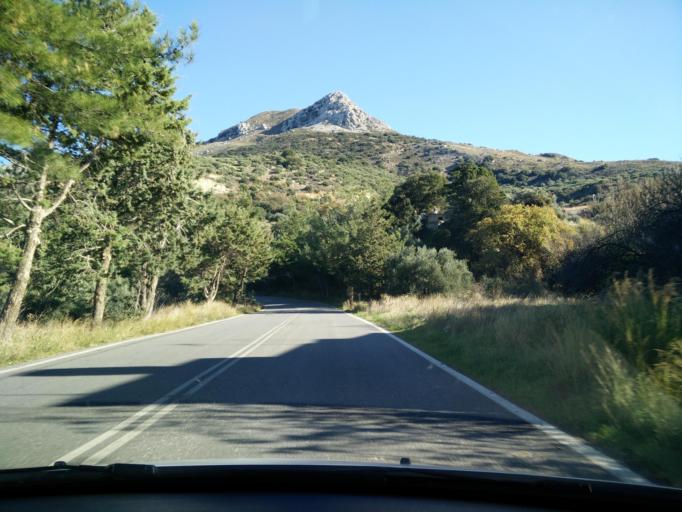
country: GR
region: Crete
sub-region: Nomos Irakleiou
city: Arkalochori
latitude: 35.0759
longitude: 25.3574
